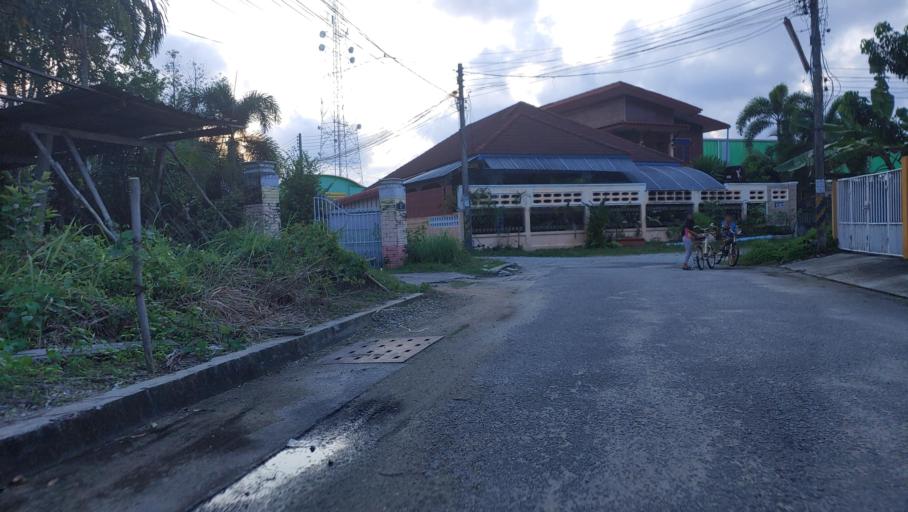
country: TH
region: Narathiwat
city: Narathiwat
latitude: 6.4389
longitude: 101.8168
